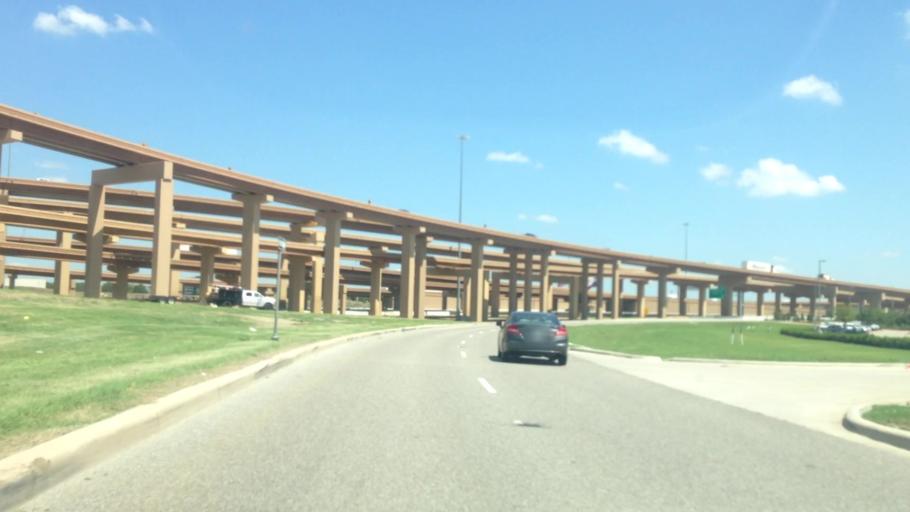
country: US
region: Texas
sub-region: Tarrant County
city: Blue Mound
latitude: 32.8372
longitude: -97.3110
